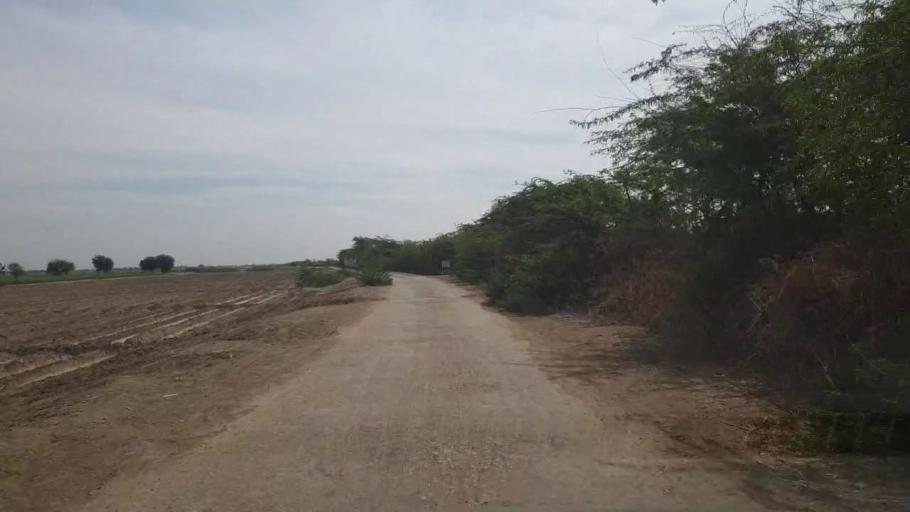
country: PK
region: Sindh
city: Kunri
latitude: 25.2740
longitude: 69.5980
